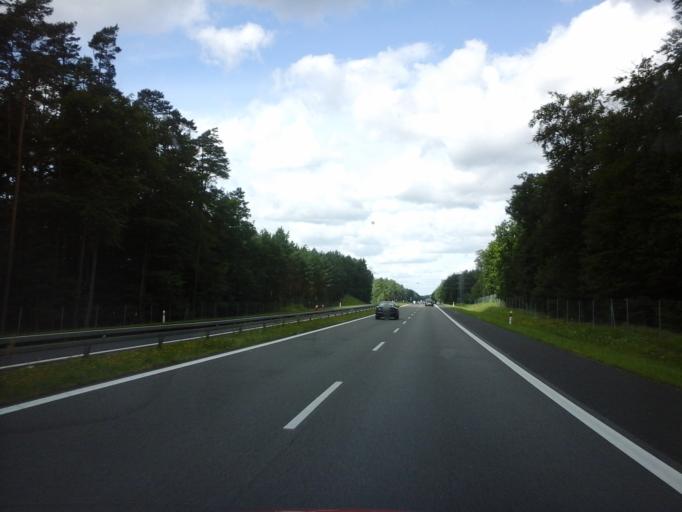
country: PL
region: West Pomeranian Voivodeship
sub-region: Powiat gryfinski
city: Stare Czarnowo
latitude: 53.3561
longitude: 14.7919
